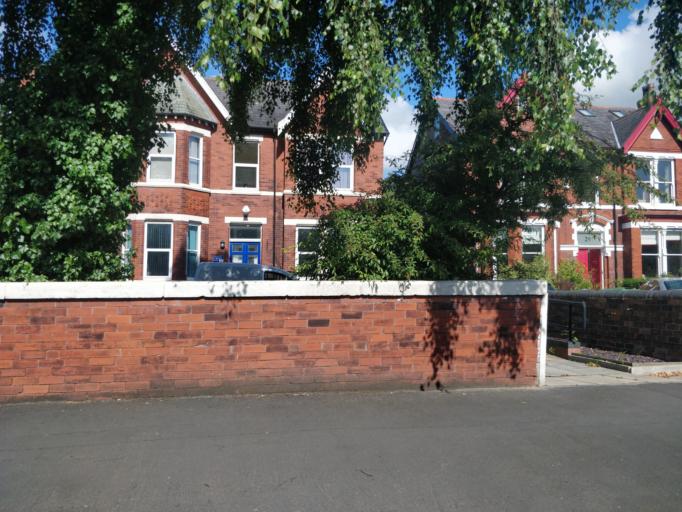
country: GB
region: England
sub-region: Sefton
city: Southport
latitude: 53.6498
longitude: -2.9776
